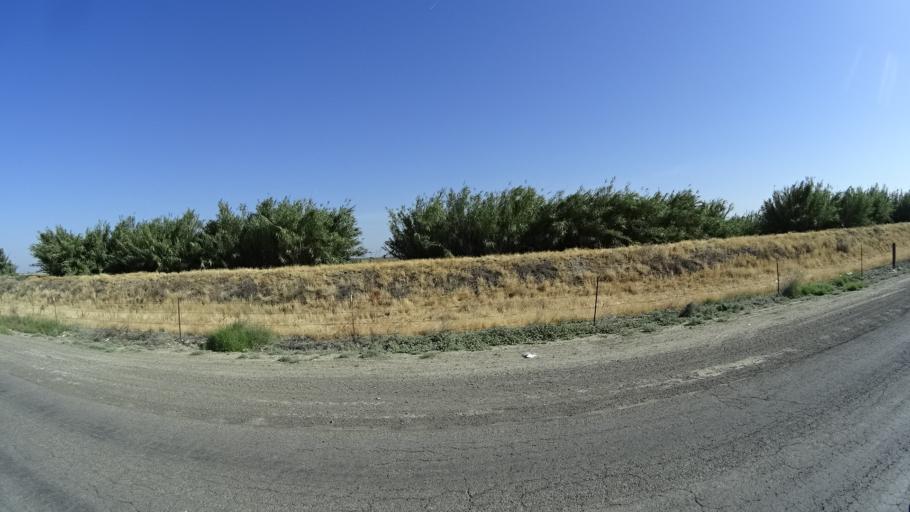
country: US
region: California
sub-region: Kings County
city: Corcoran
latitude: 36.1379
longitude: -119.5459
